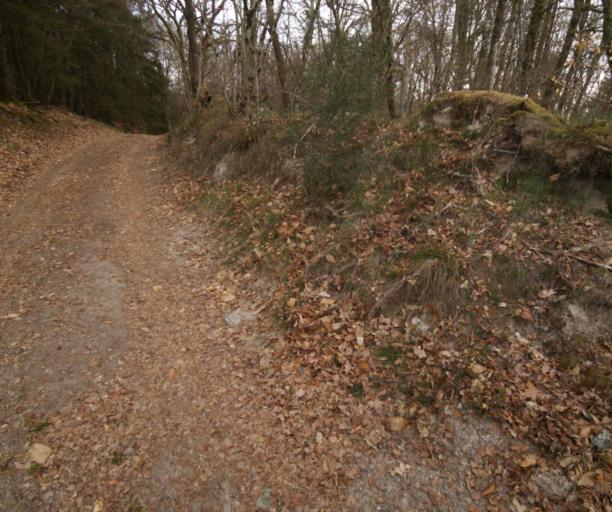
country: FR
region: Limousin
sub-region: Departement de la Correze
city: Correze
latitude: 45.4315
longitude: 1.8541
